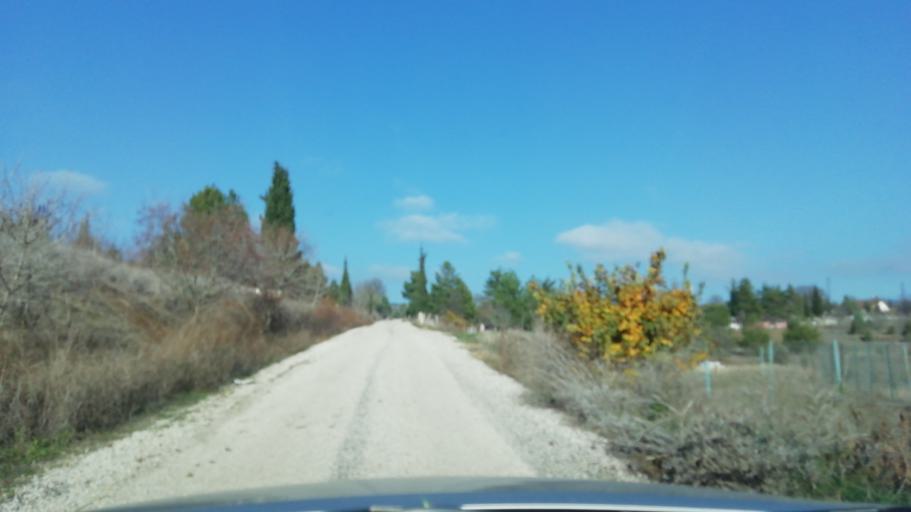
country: TR
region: Karabuk
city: Safranbolu
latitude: 41.2289
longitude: 32.7764
